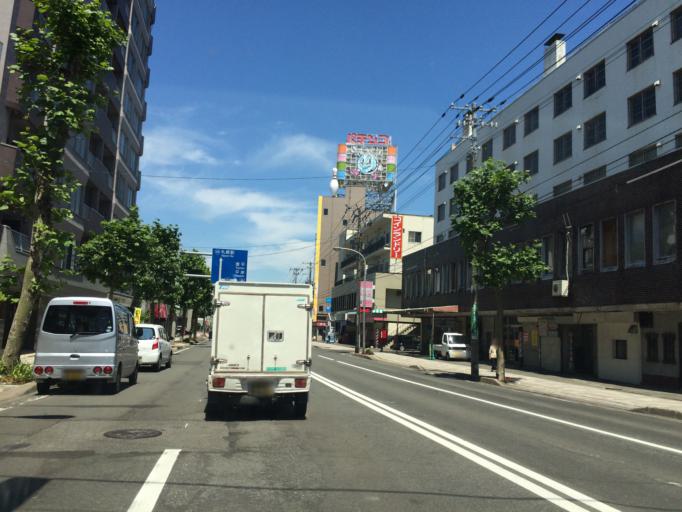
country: JP
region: Hokkaido
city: Sapporo
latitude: 43.0038
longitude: 141.3482
